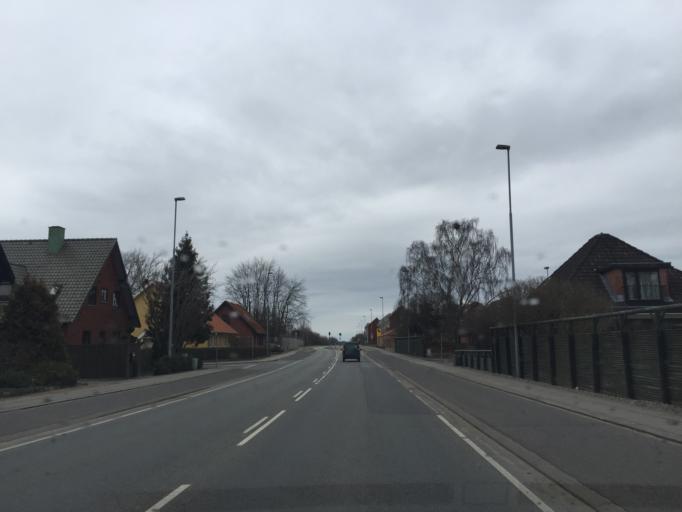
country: DK
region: South Denmark
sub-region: Odense Kommune
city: Odense
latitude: 55.3970
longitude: 10.3396
